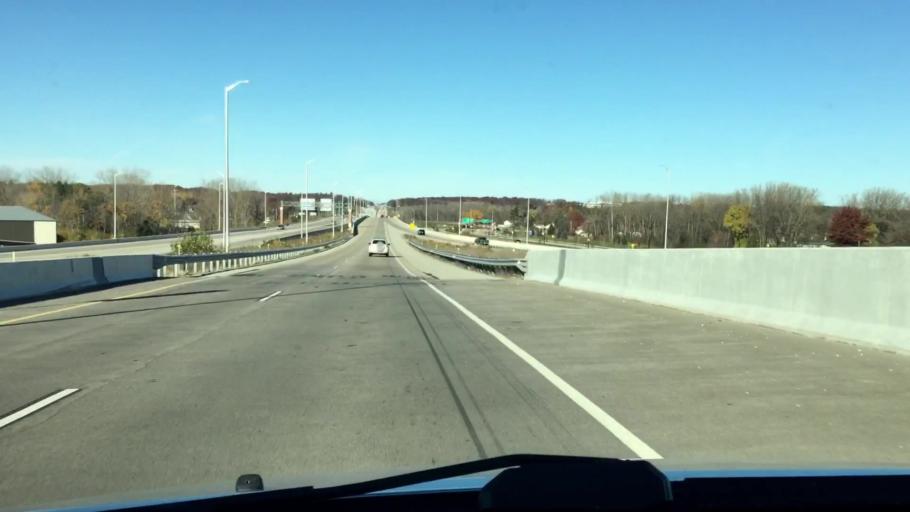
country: US
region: Wisconsin
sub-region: Brown County
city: Howard
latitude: 44.5403
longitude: -88.0812
